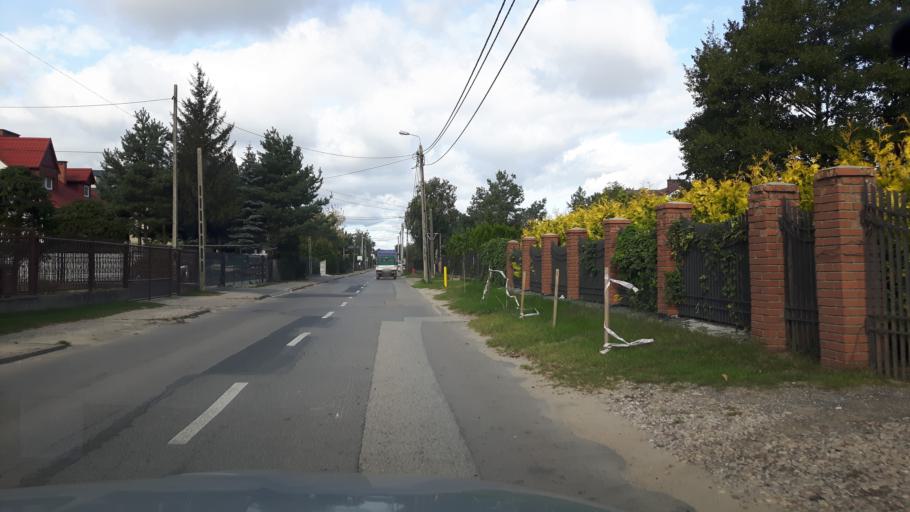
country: PL
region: Masovian Voivodeship
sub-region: Powiat wolominski
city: Marki
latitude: 52.3230
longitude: 21.1114
